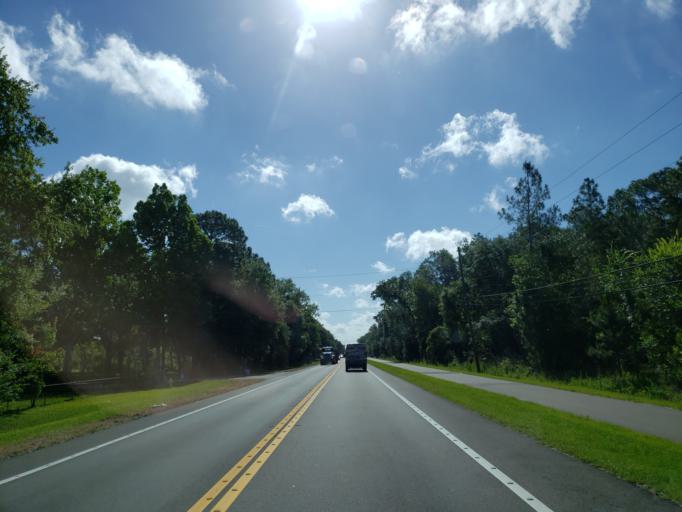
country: US
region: Florida
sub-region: Pasco County
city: Trinity
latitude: 28.1448
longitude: -82.6799
